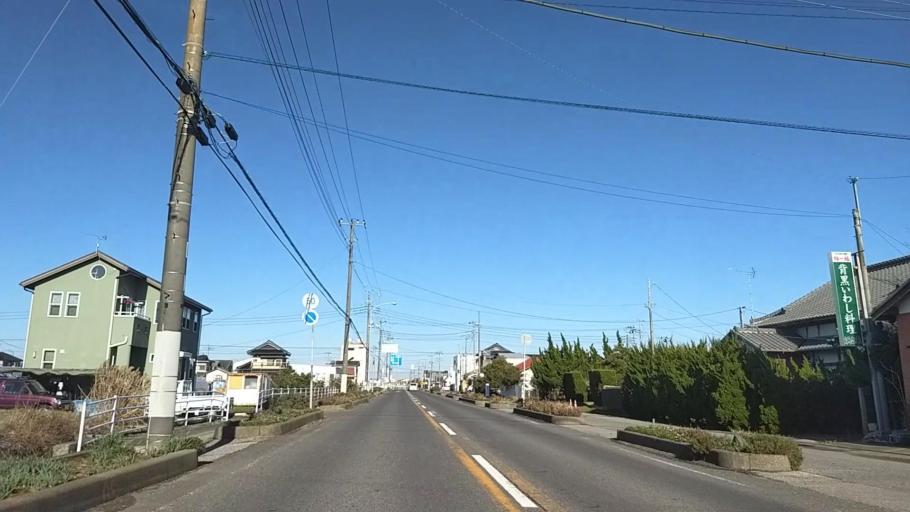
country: JP
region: Chiba
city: Naruto
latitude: 35.5364
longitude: 140.4538
